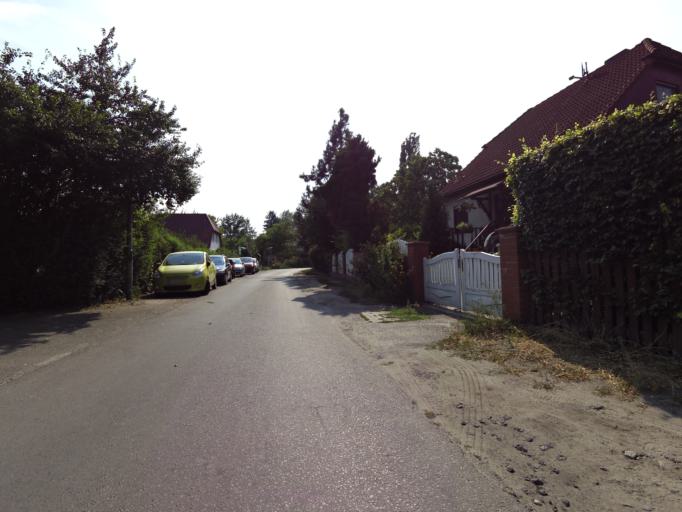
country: DE
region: Berlin
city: Altglienicke
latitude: 52.4207
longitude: 13.5442
